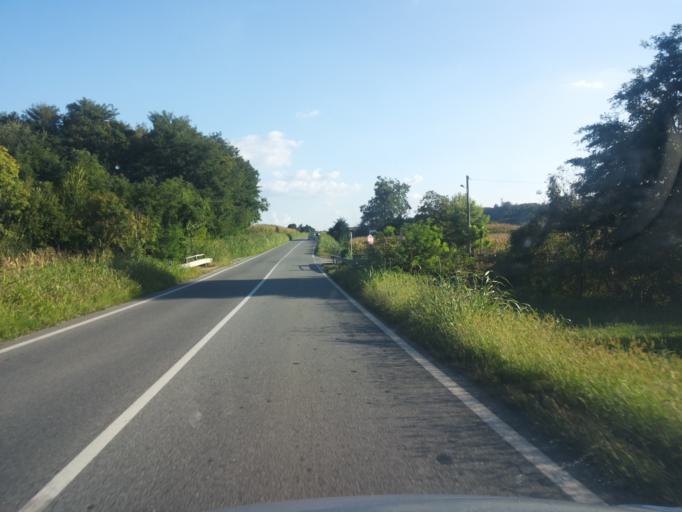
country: IT
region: Piedmont
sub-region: Provincia di Torino
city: Romano Canavese
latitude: 45.4024
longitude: 7.8833
